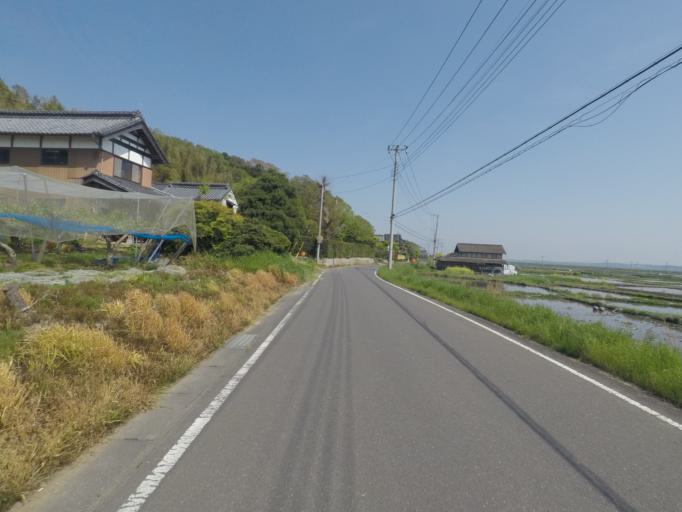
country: JP
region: Ibaraki
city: Ami
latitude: 36.0697
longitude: 140.2806
